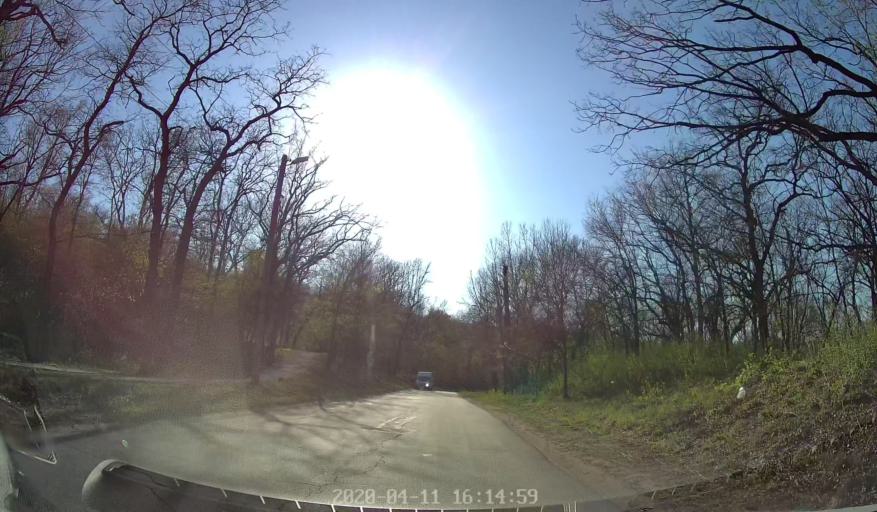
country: MD
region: Chisinau
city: Vadul lui Voda
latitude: 47.0777
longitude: 29.0971
